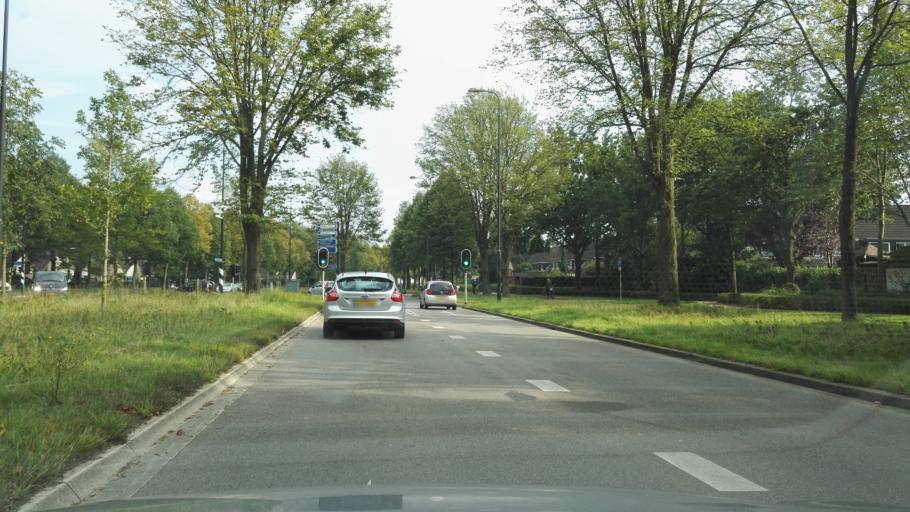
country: NL
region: Gelderland
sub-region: Gemeente Apeldoorn
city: Apeldoorn
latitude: 52.2022
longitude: 5.9965
